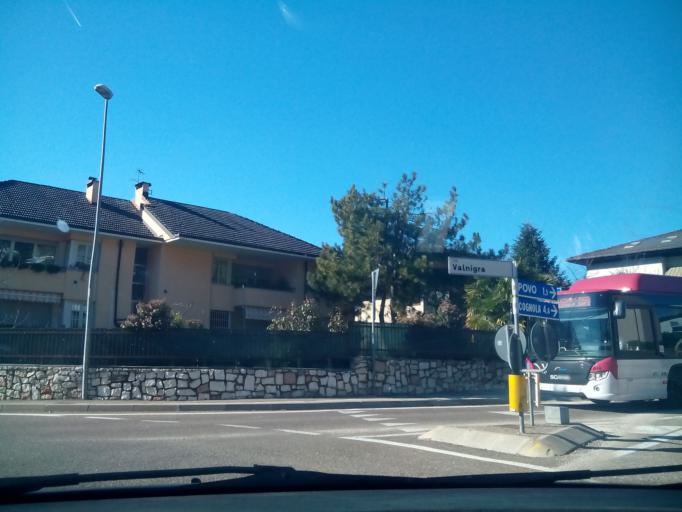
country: IT
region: Trentino-Alto Adige
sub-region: Provincia di Trento
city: Povo
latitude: 46.0496
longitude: 11.1450
